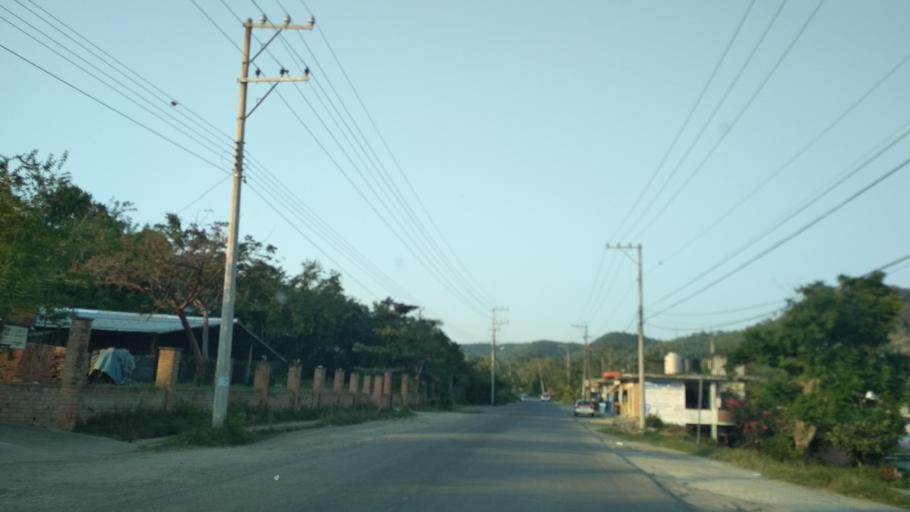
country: MM
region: Shan
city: Taunggyi
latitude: 20.4103
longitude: 97.3370
